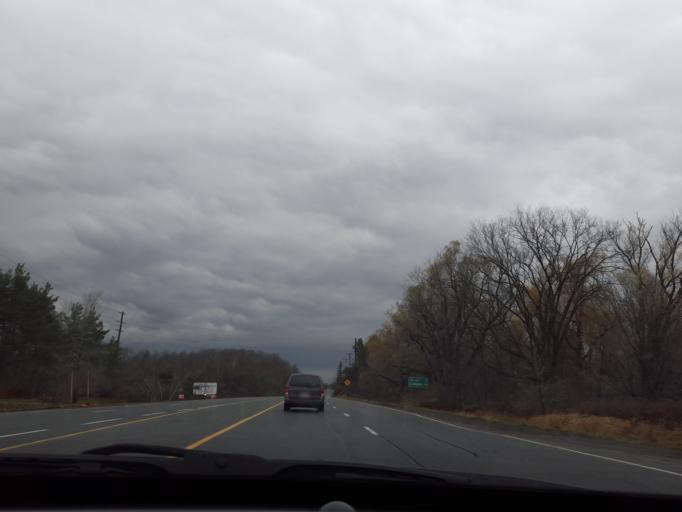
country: CA
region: Ontario
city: Pickering
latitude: 43.8886
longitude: -79.0916
